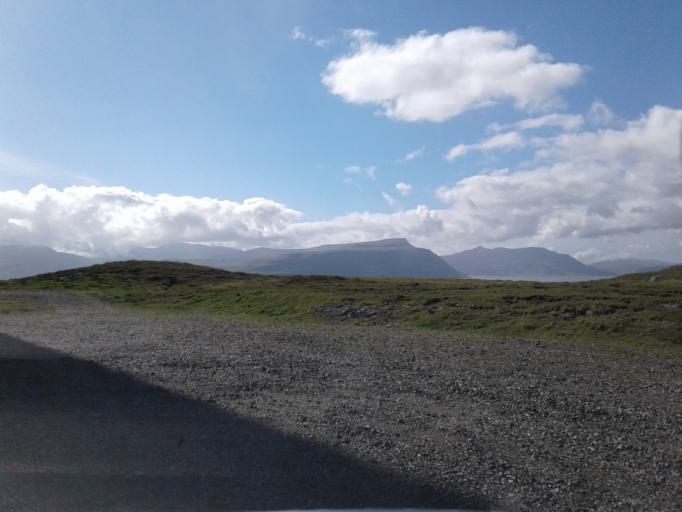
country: FO
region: Streymoy
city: Hoyvik
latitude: 62.0582
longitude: -6.6957
